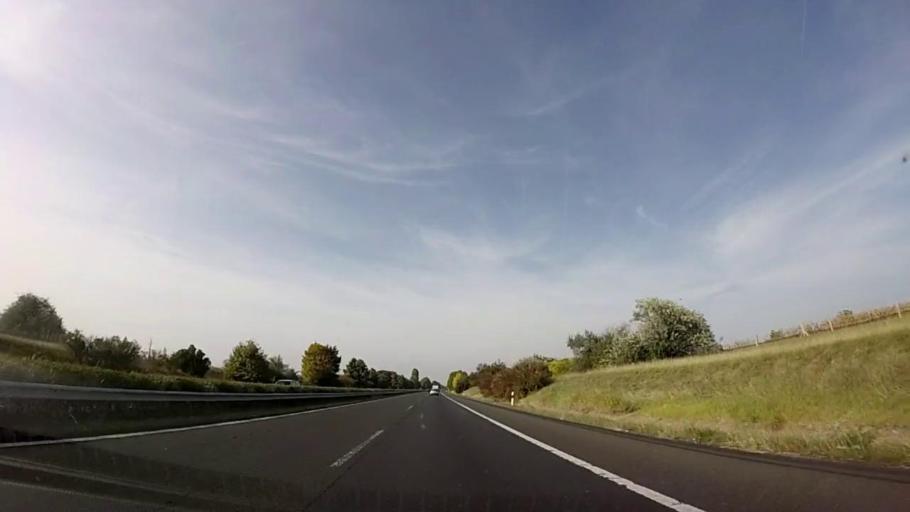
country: HU
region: Somogy
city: Siofok
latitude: 46.8876
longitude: 18.0319
